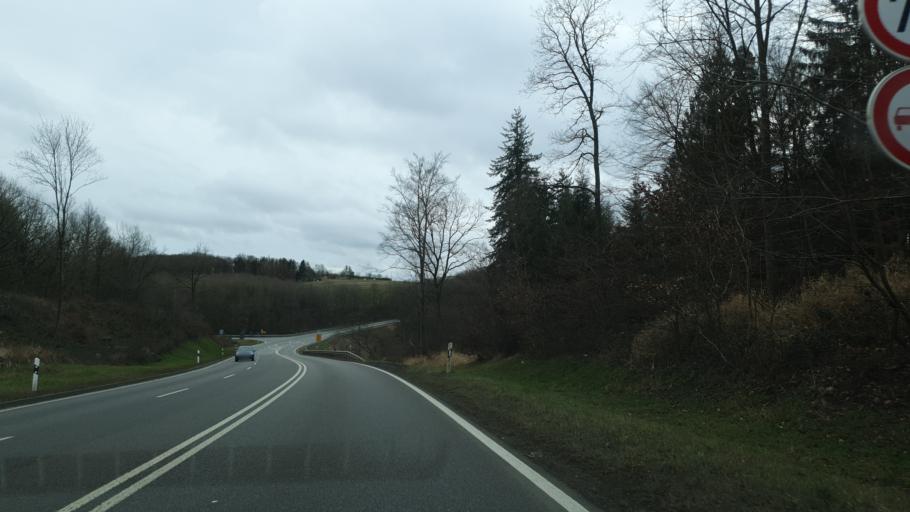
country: DE
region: Rheinland-Pfalz
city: Kratzenburg
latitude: 50.1846
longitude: 7.5705
